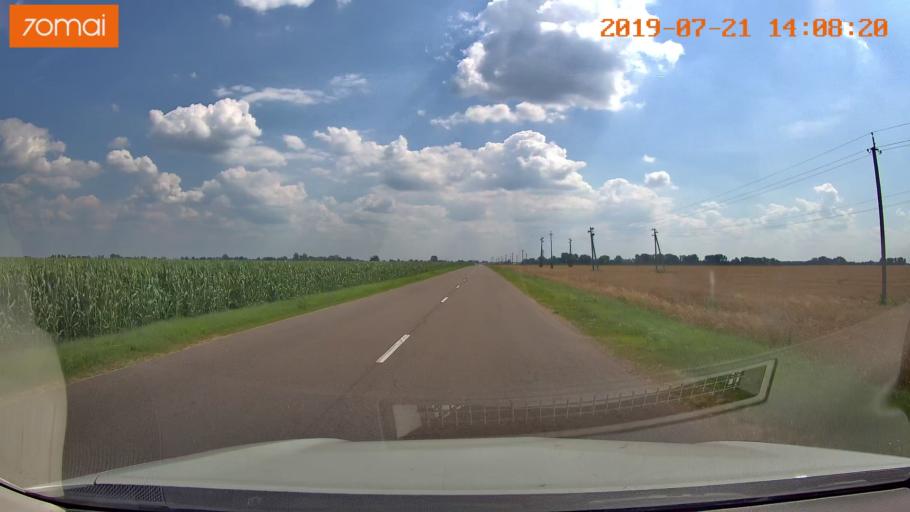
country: BY
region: Grodnenskaya
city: Lyubcha
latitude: 53.6740
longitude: 26.1247
